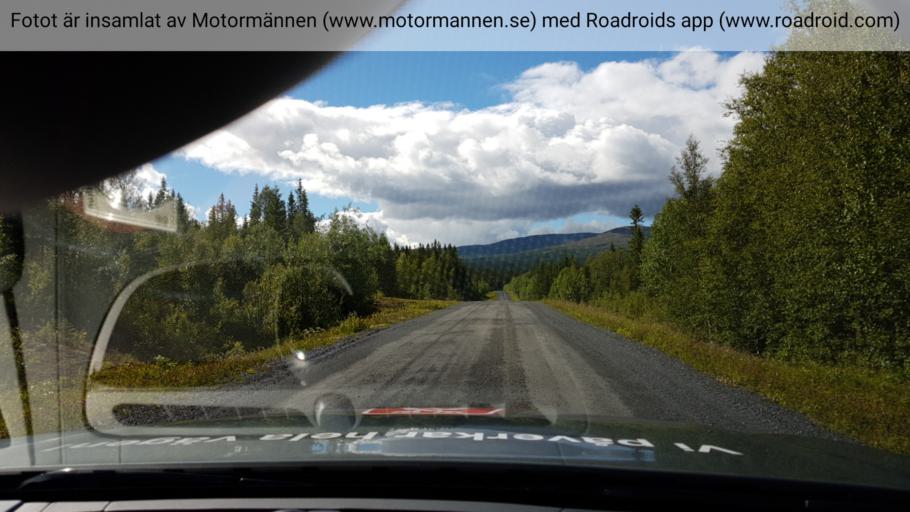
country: SE
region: Jaemtland
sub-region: Krokoms Kommun
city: Valla
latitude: 63.0973
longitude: 13.8909
